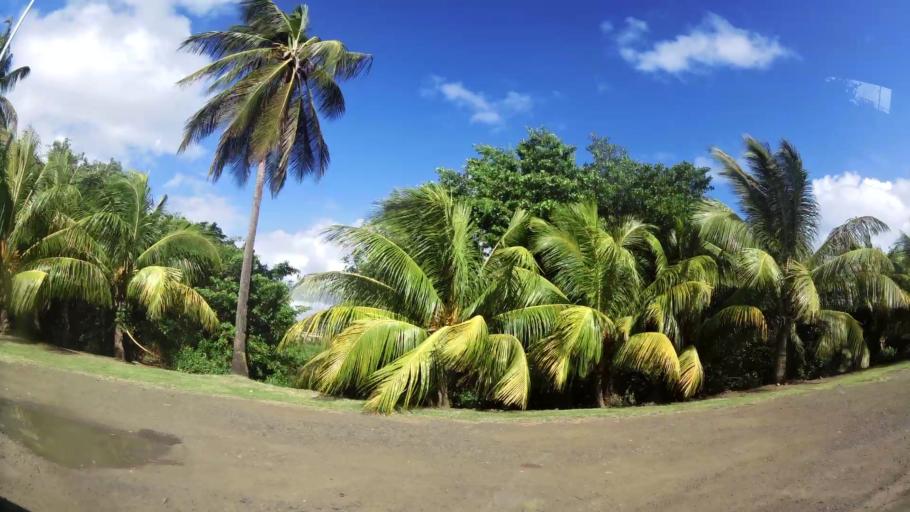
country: MQ
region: Martinique
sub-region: Martinique
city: Le Francois
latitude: 14.6169
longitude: -60.9082
